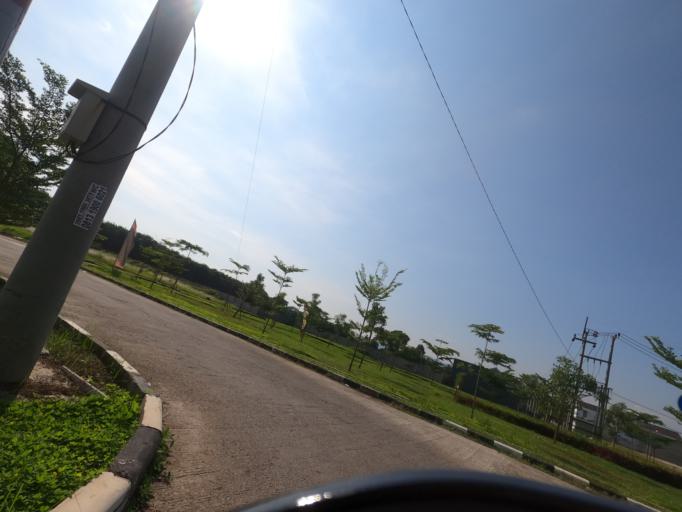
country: ID
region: West Java
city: Lembang
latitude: -6.5762
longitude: 107.7913
